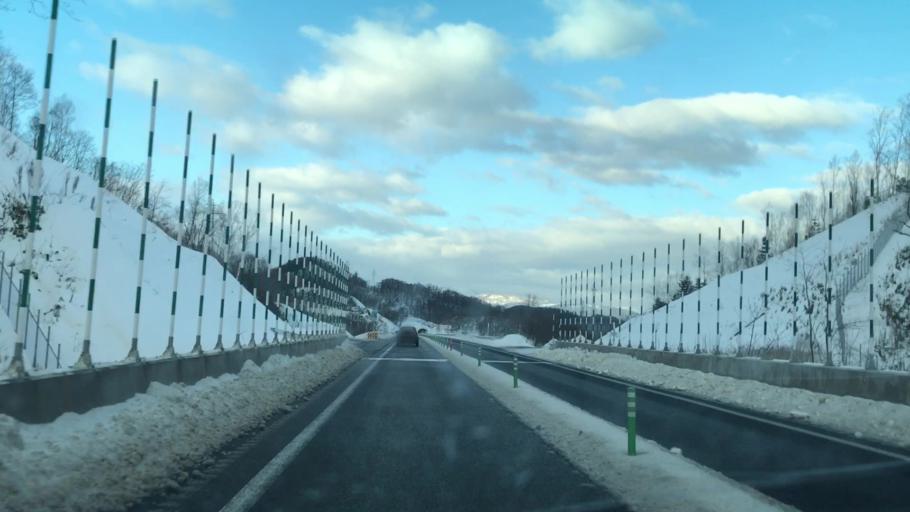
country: JP
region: Hokkaido
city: Otaru
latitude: 43.1966
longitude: 140.9068
